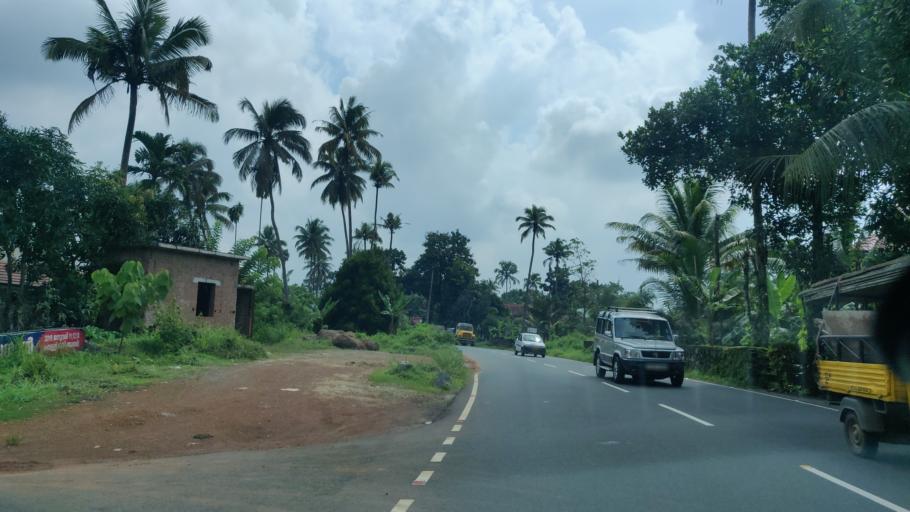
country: IN
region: Kerala
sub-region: Ernakulam
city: Angamali
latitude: 10.1673
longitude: 76.4176
